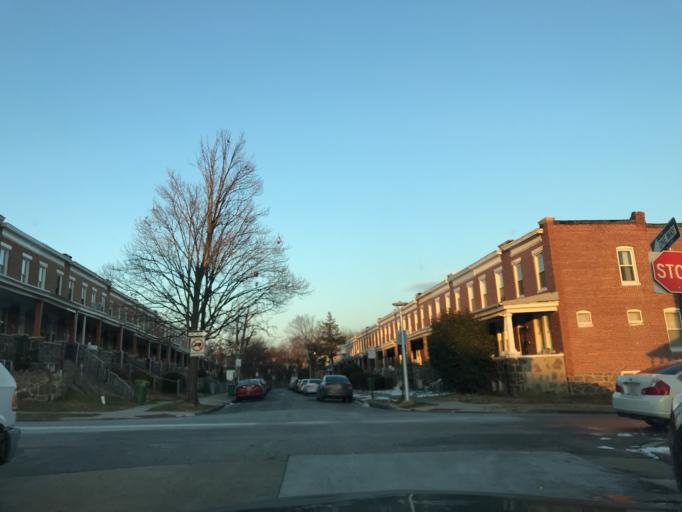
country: US
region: Maryland
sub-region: City of Baltimore
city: Baltimore
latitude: 39.3200
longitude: -76.5989
